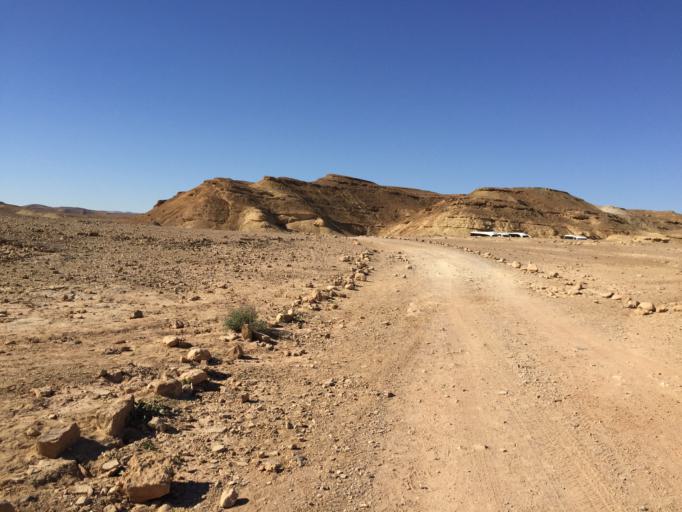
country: IL
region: Southern District
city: Mitzpe Ramon
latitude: 30.6050
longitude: 34.9394
